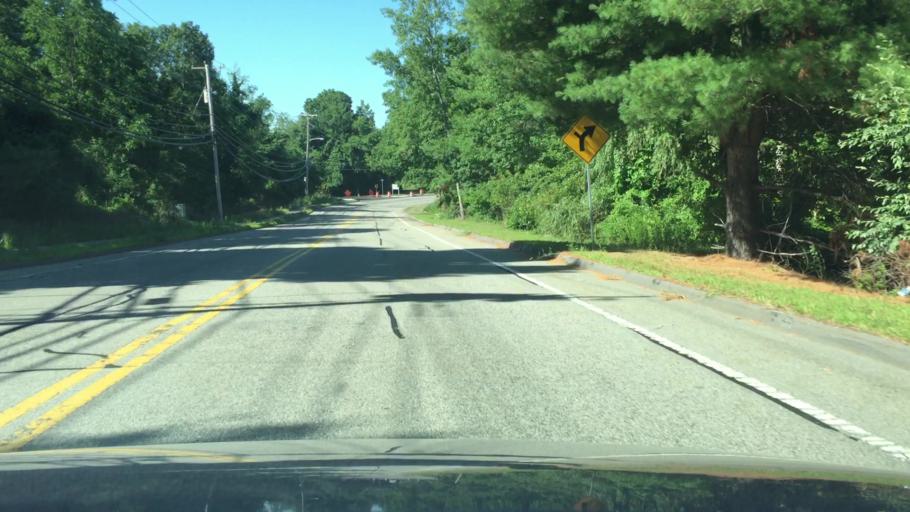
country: US
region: Massachusetts
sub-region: Middlesex County
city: Marlborough
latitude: 42.3256
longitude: -71.5903
